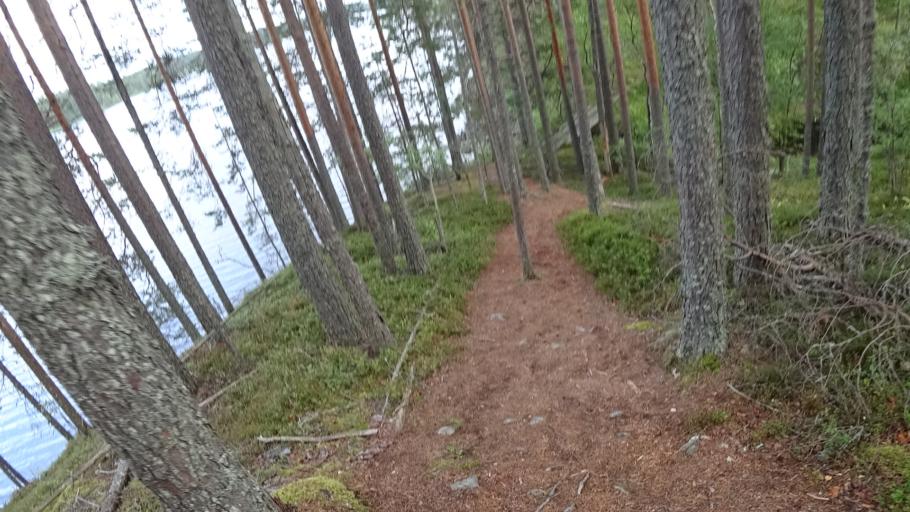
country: FI
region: North Karelia
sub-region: Joensuu
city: Ilomantsi
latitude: 62.5763
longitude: 31.1729
